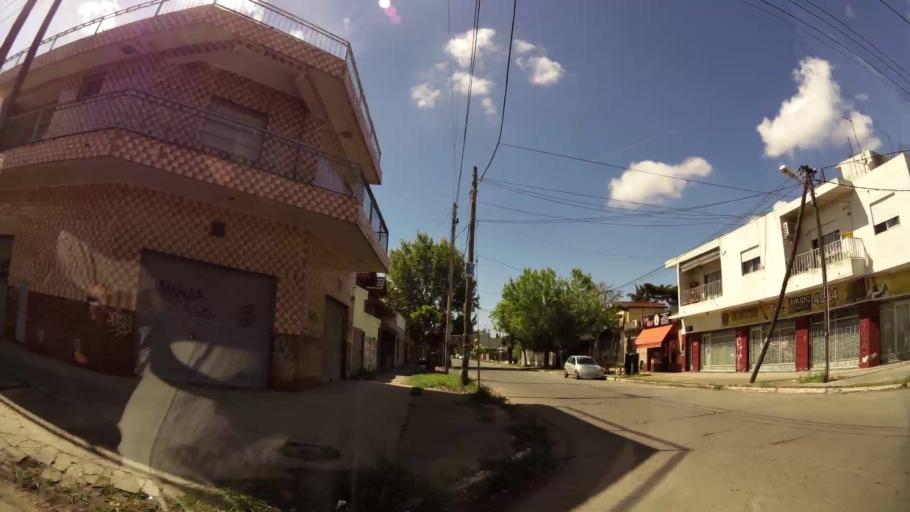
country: AR
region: Buenos Aires
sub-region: Partido de Quilmes
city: Quilmes
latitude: -34.8158
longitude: -58.2743
